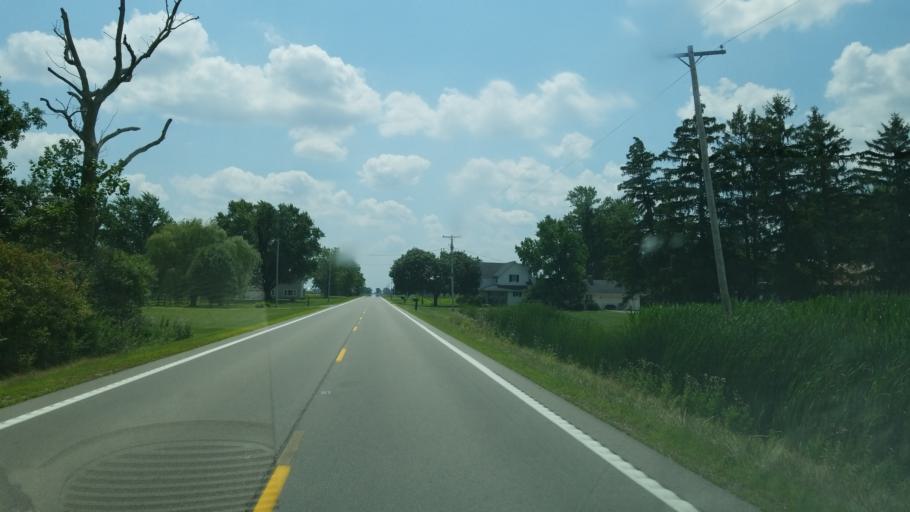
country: US
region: Ohio
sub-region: Henry County
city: Deshler
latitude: 41.2713
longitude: -83.9406
